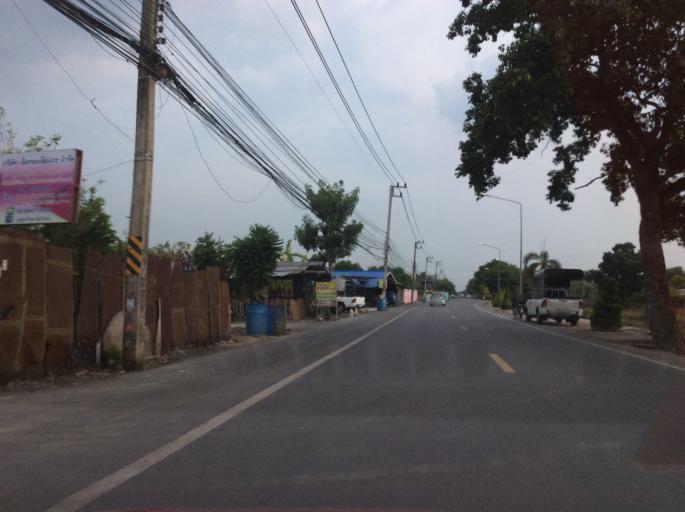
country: TH
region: Pathum Thani
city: Lam Luk Ka
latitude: 13.9599
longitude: 100.7275
